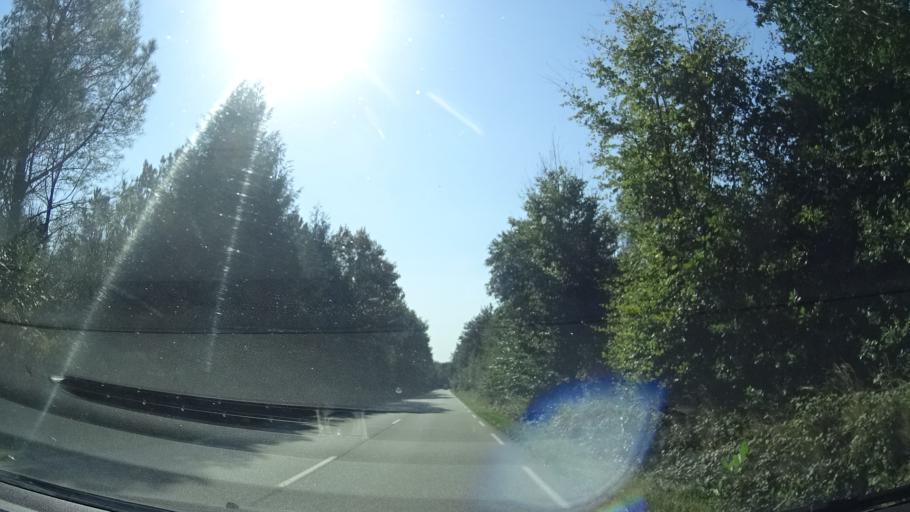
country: FR
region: Brittany
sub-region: Departement du Finistere
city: Cast
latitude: 48.1743
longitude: -4.1241
